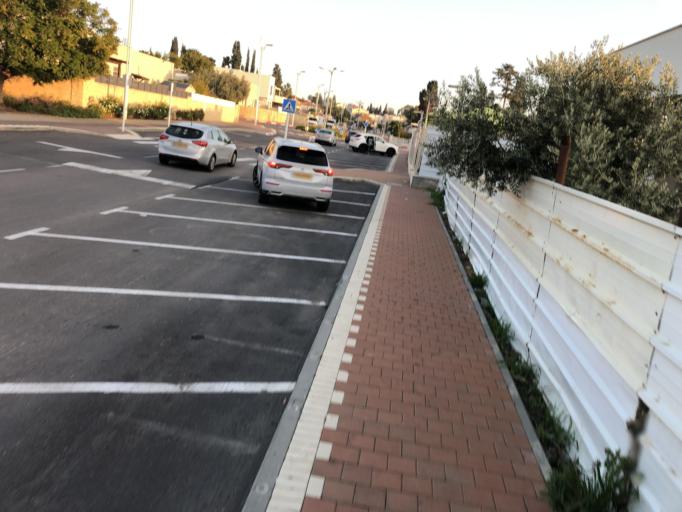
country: IL
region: Northern District
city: `Akko
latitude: 32.9282
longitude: 35.0858
